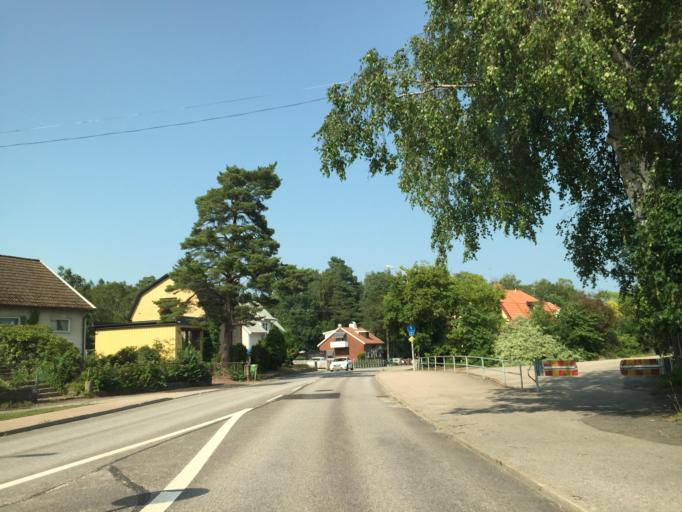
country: SE
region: Vaestra Goetaland
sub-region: Vanersborgs Kommun
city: Vanersborg
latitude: 58.3810
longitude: 12.2952
